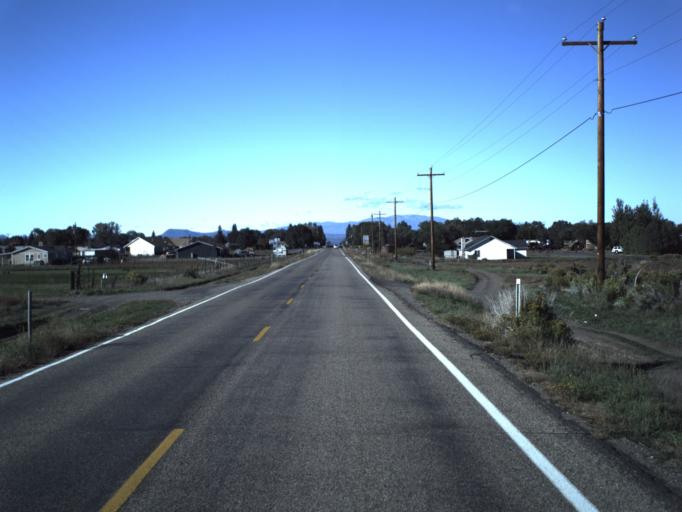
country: US
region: Utah
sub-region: Garfield County
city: Panguitch
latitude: 37.8108
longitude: -112.4354
